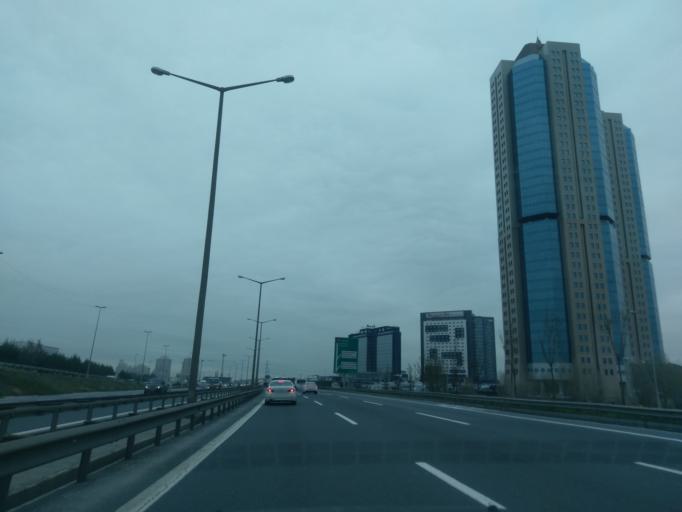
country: TR
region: Istanbul
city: Esenler
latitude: 41.0686
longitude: 28.8618
